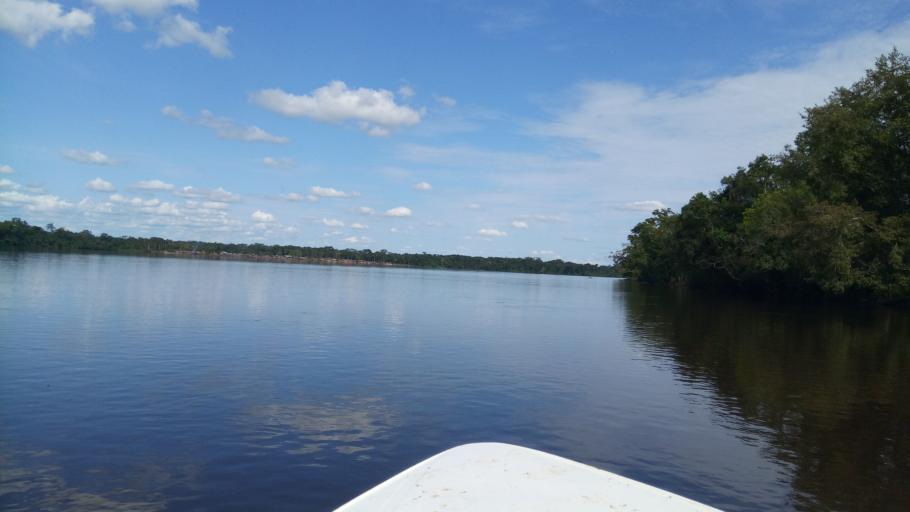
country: CD
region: Eastern Province
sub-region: Sous-Region de la Tshopo
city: Yangambi
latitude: 0.5528
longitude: 24.2397
